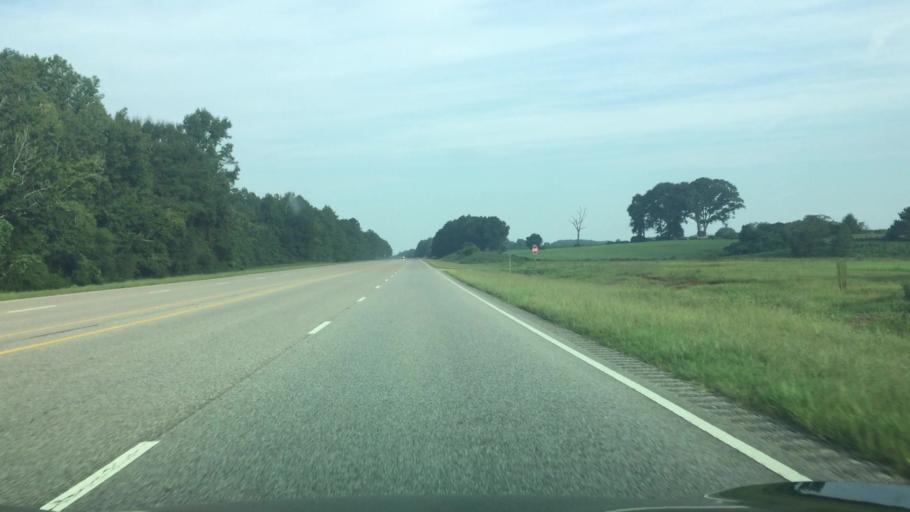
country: US
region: Alabama
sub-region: Covington County
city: Andalusia
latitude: 31.3988
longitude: -86.5795
